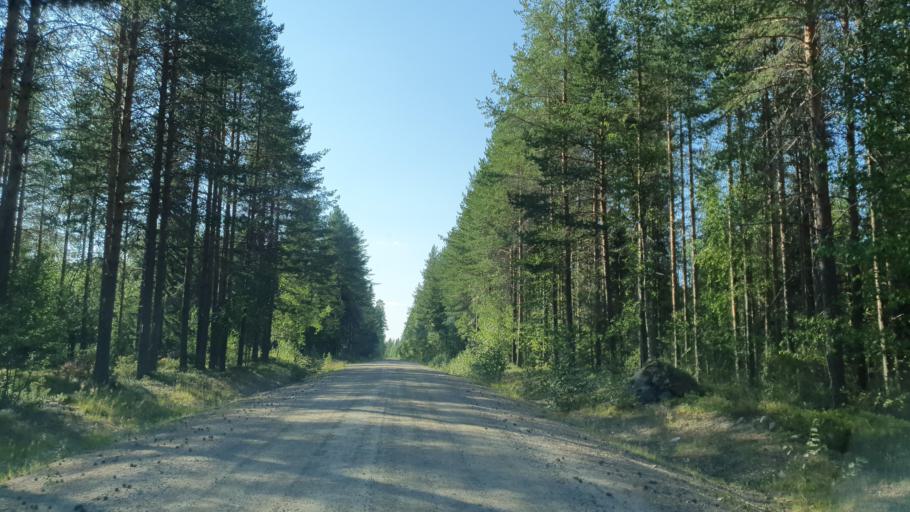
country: FI
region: Kainuu
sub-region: Kehys-Kainuu
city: Kuhmo
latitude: 64.0241
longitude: 29.7241
